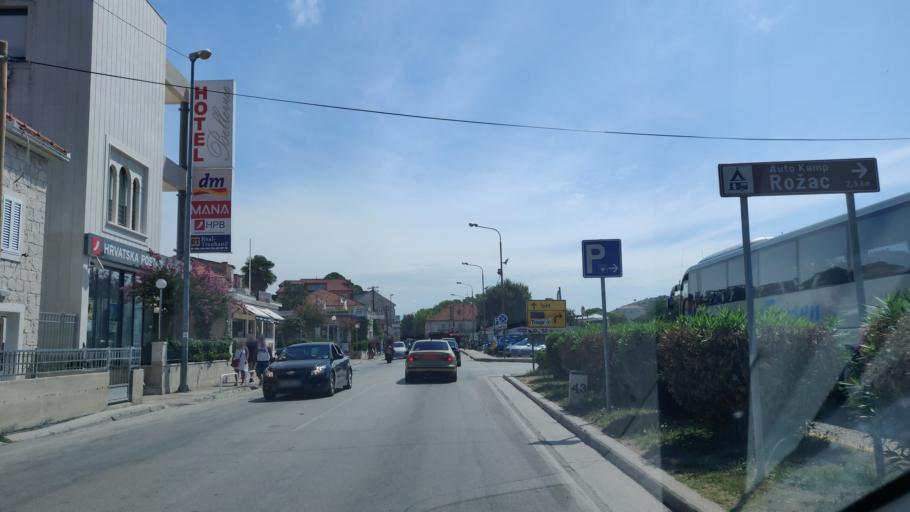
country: HR
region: Splitsko-Dalmatinska
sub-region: Grad Trogir
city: Trogir
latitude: 43.5185
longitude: 16.2474
